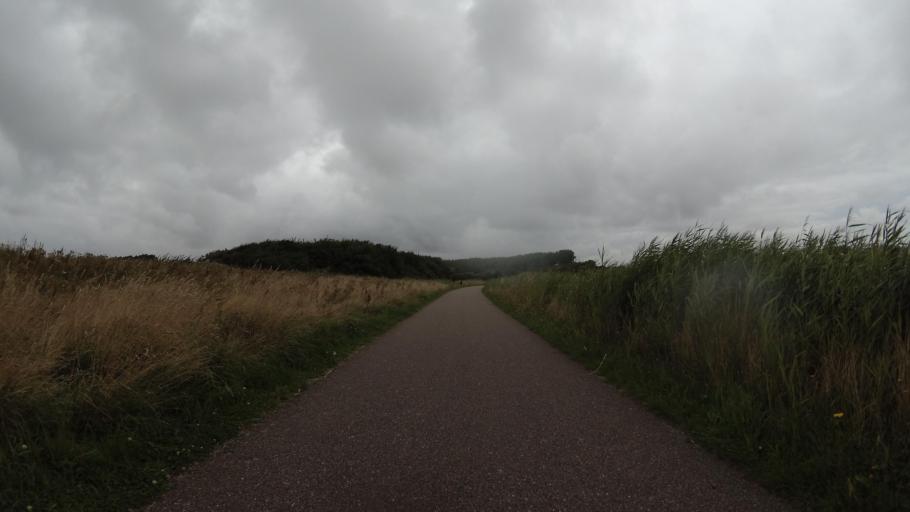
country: NL
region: North Holland
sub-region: Gemeente Den Helder
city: Den Helder
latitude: 52.9290
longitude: 4.7373
